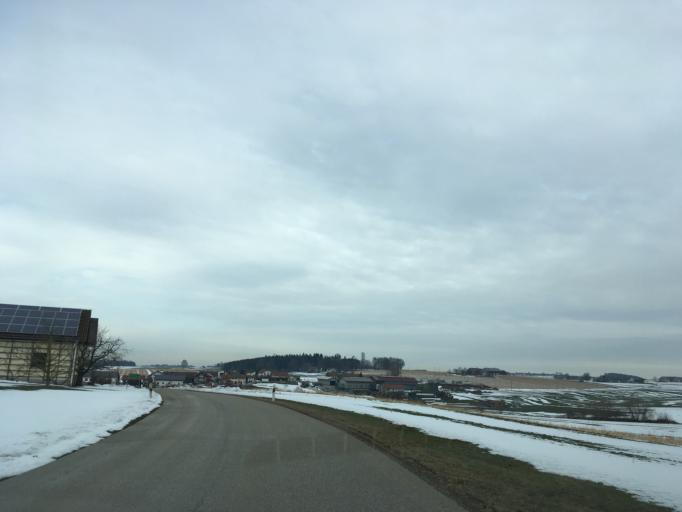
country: DE
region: Bavaria
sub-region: Upper Bavaria
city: Jettenbach
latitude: 48.1218
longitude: 12.3832
